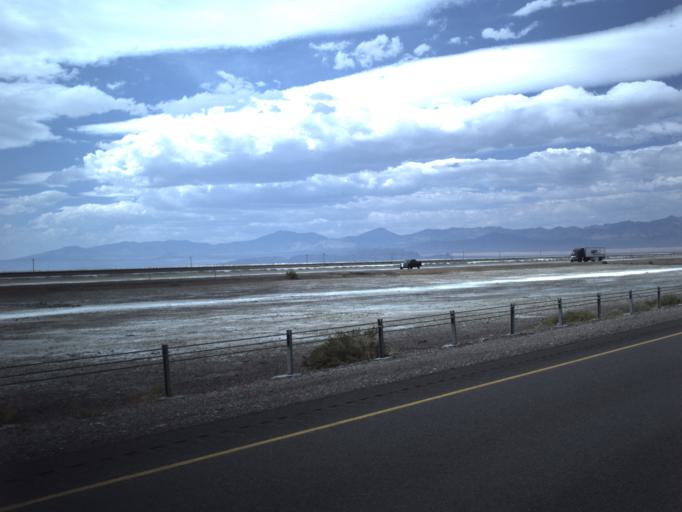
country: US
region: Utah
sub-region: Tooele County
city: Wendover
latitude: 40.7405
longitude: -113.9084
